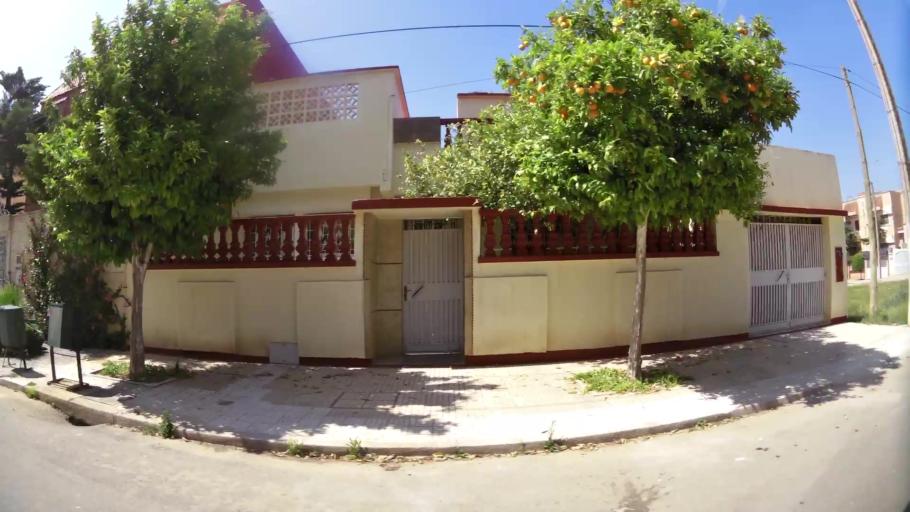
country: MA
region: Oriental
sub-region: Oujda-Angad
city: Oujda
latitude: 34.6856
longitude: -1.8770
